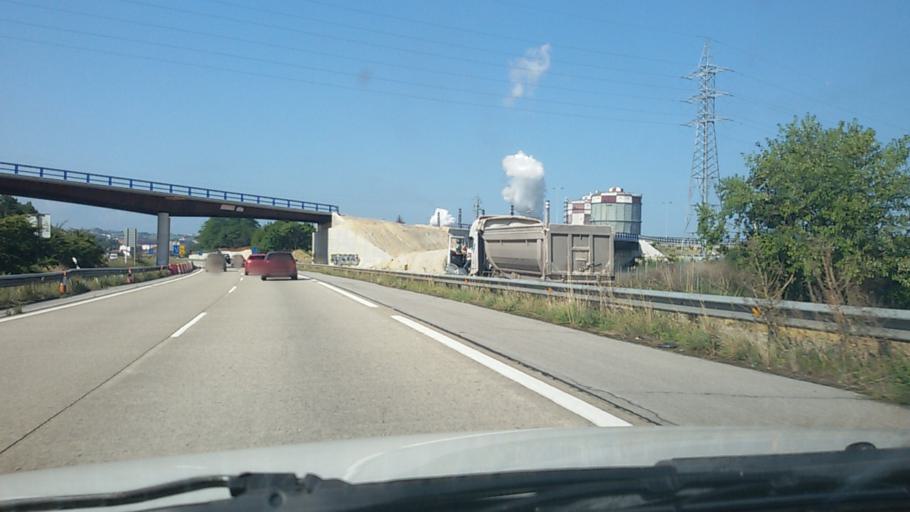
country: ES
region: Asturias
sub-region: Province of Asturias
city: Aviles
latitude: 43.5536
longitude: -5.8895
